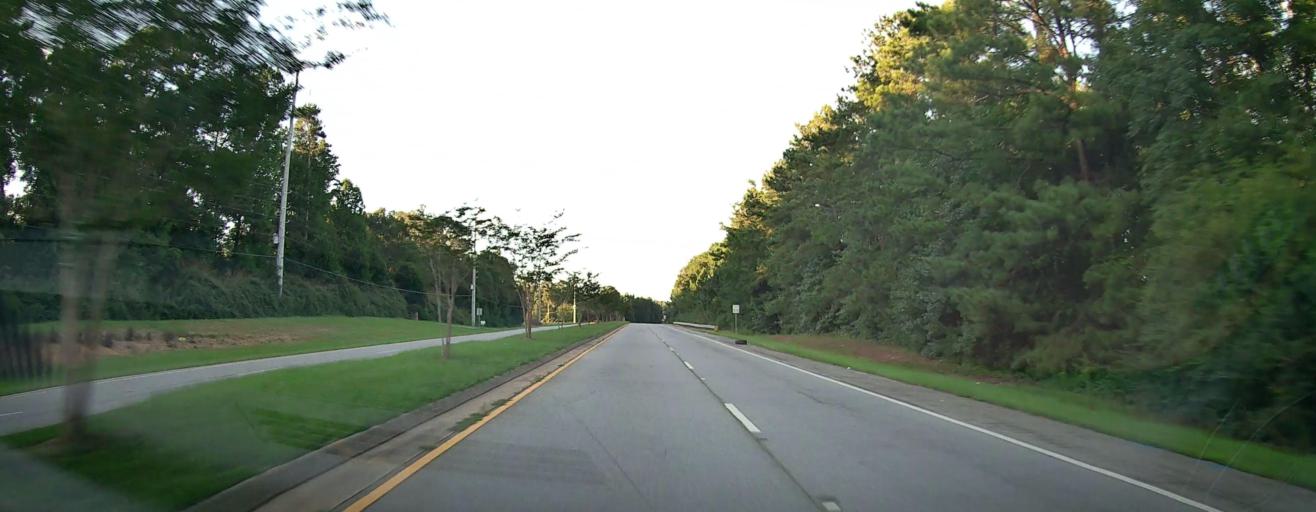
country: US
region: Georgia
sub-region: Muscogee County
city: Columbus
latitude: 32.5302
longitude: -84.8535
